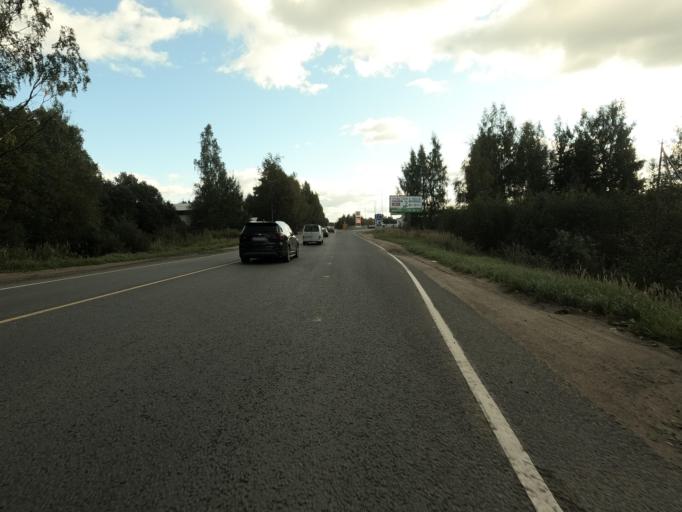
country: RU
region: Leningrad
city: Vsevolozhsk
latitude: 59.9783
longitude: 30.6538
